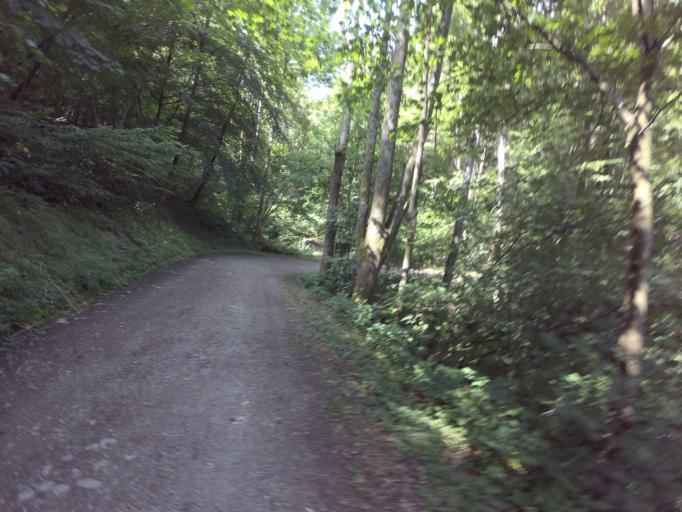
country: DE
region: North Rhine-Westphalia
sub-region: Regierungsbezirk Koln
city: Simmerath
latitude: 50.5923
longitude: 6.3772
